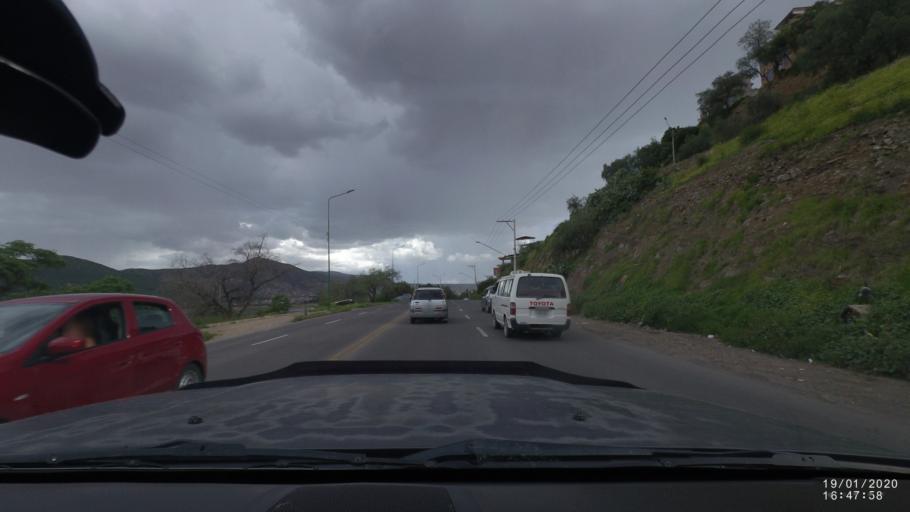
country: BO
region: Cochabamba
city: Cochabamba
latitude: -17.4077
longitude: -66.1439
